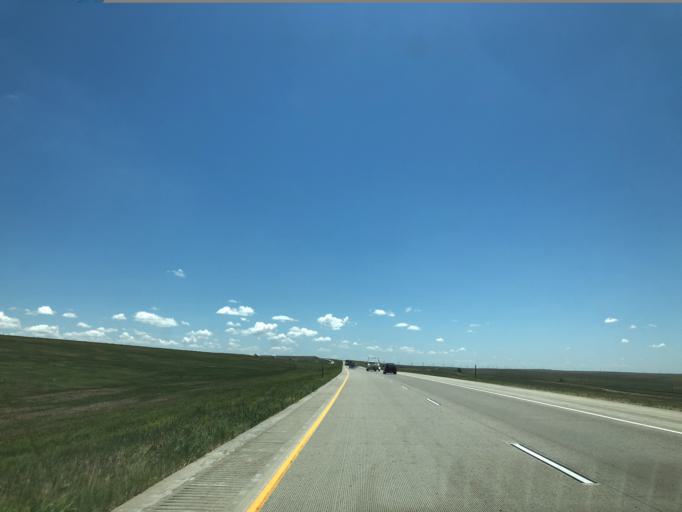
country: US
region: Colorado
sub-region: Lincoln County
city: Limon
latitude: 39.3807
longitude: -103.8885
